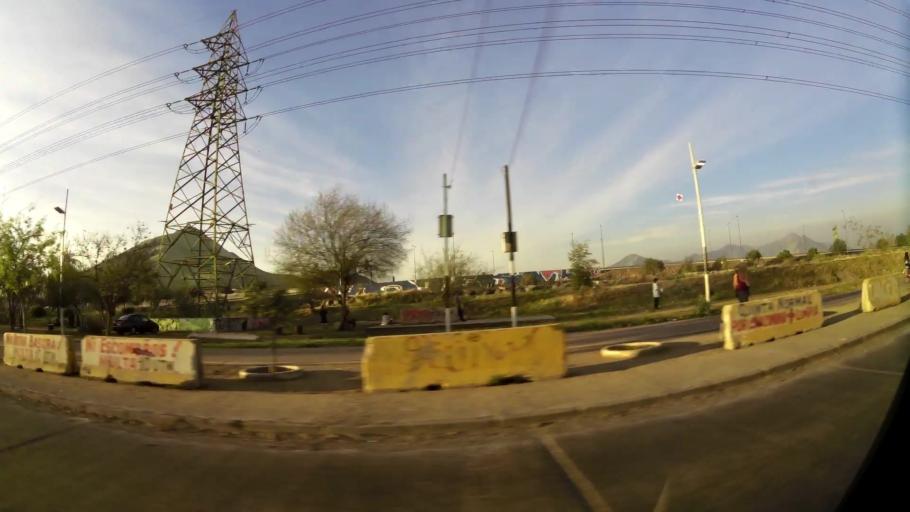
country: CL
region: Santiago Metropolitan
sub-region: Provincia de Santiago
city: Lo Prado
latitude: -33.4089
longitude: -70.7039
